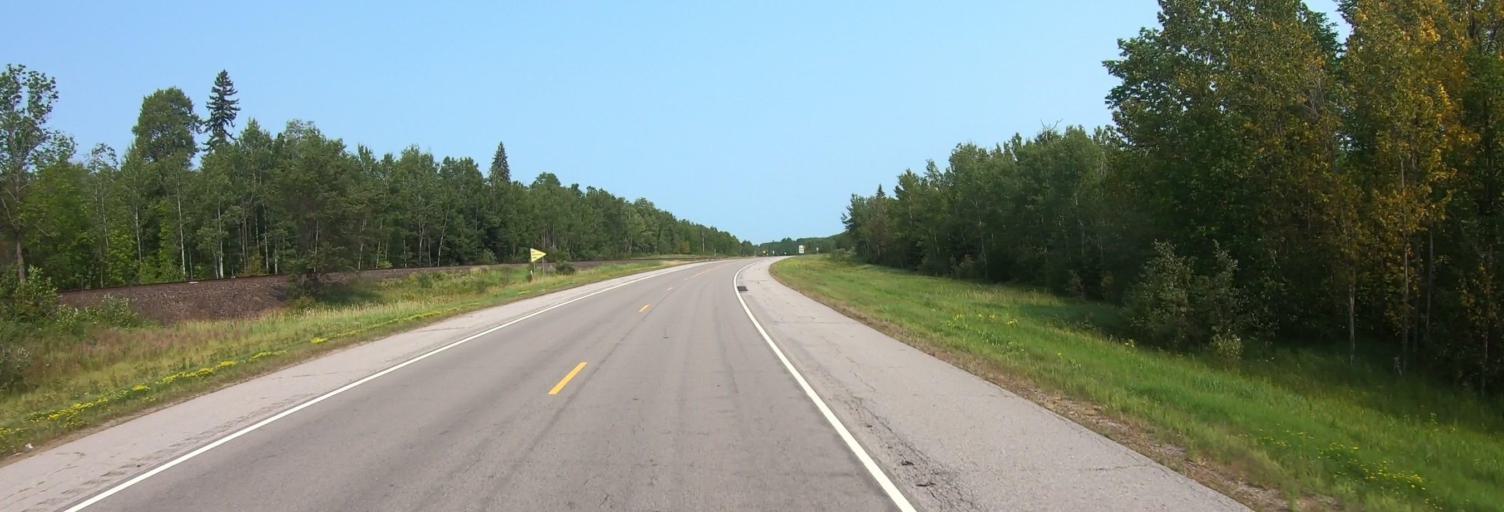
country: CA
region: Ontario
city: Fort Frances
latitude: 48.2310
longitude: -92.9265
